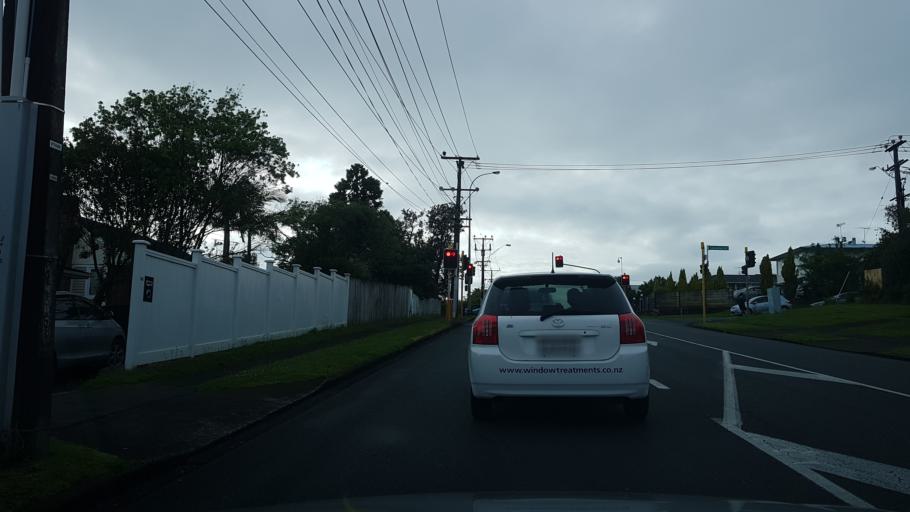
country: NZ
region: Auckland
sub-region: Auckland
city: North Shore
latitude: -36.7864
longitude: 174.7415
